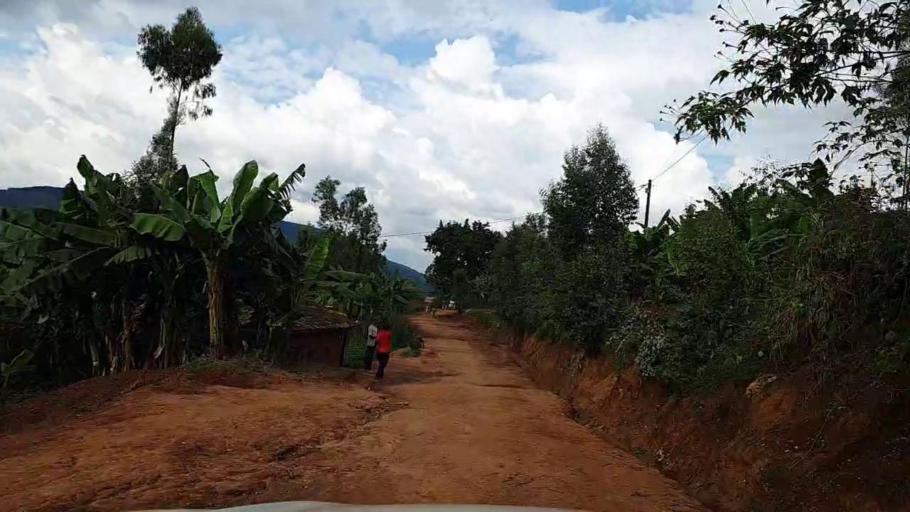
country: RW
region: Southern Province
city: Gikongoro
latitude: -2.4239
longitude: 29.6466
